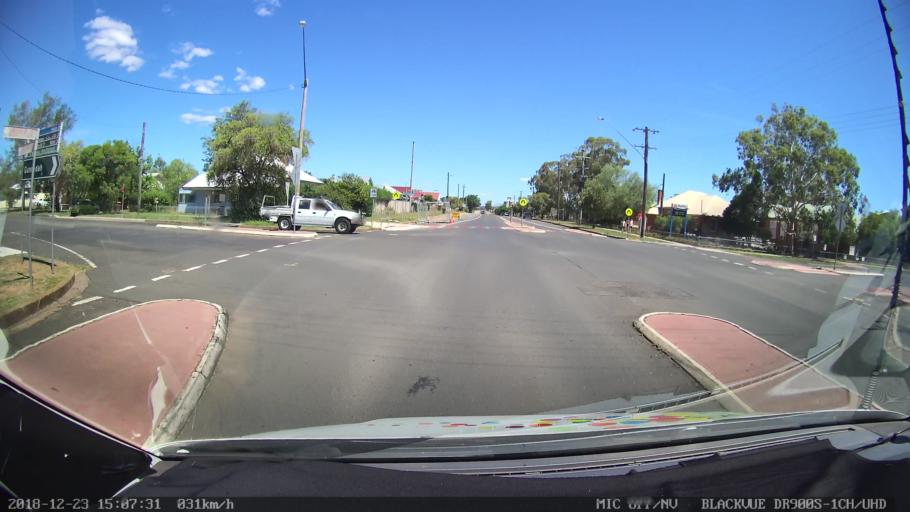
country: AU
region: New South Wales
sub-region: Tamworth Municipality
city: Manilla
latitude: -30.7482
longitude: 150.7245
